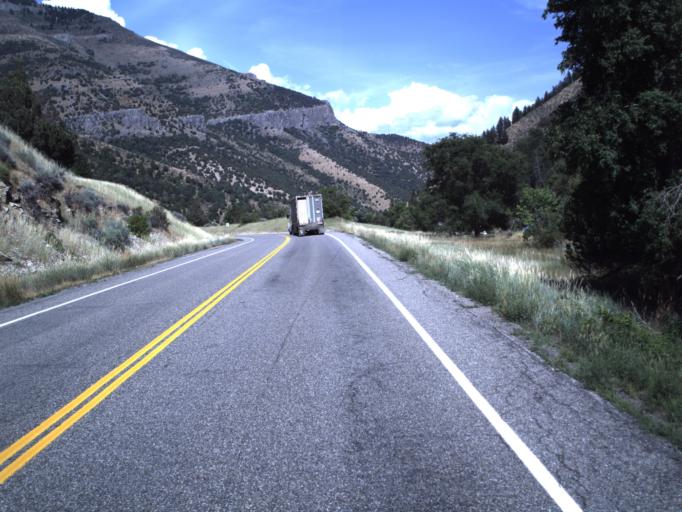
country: US
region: Utah
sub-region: Cache County
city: North Logan
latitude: 41.7568
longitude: -111.7115
